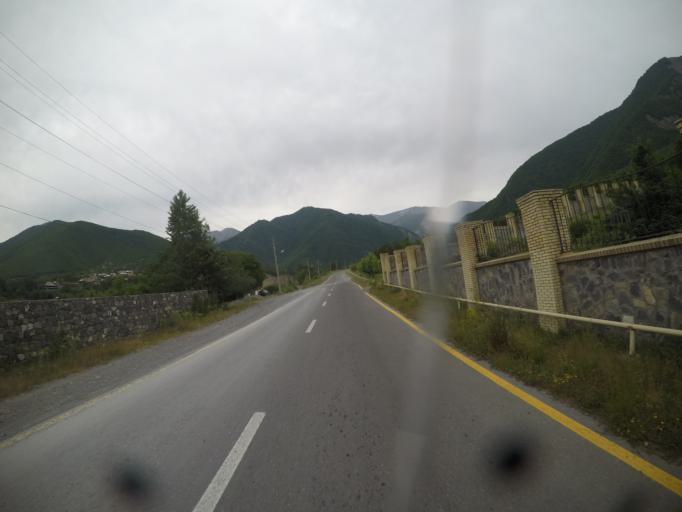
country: AZ
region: Shaki City
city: Sheki
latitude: 41.2480
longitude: 47.2019
